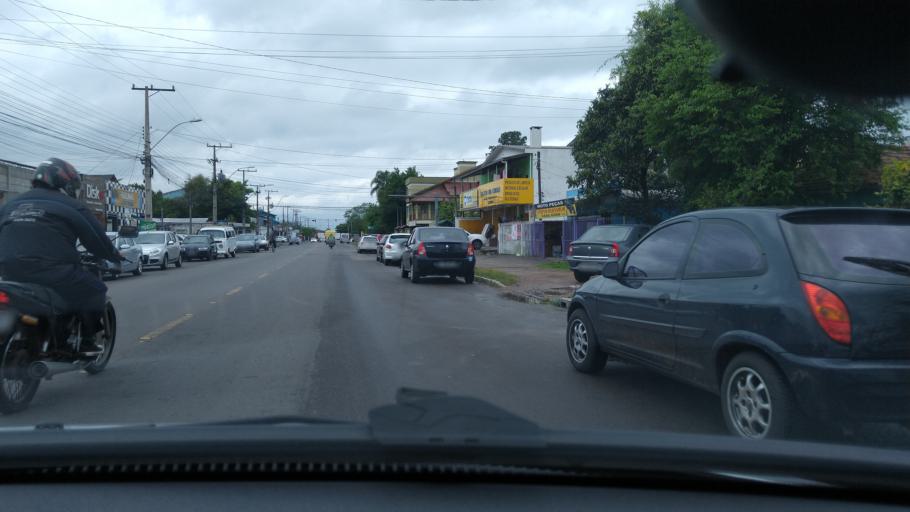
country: BR
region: Rio Grande do Sul
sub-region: Canoas
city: Canoas
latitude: -29.9018
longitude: -51.2090
